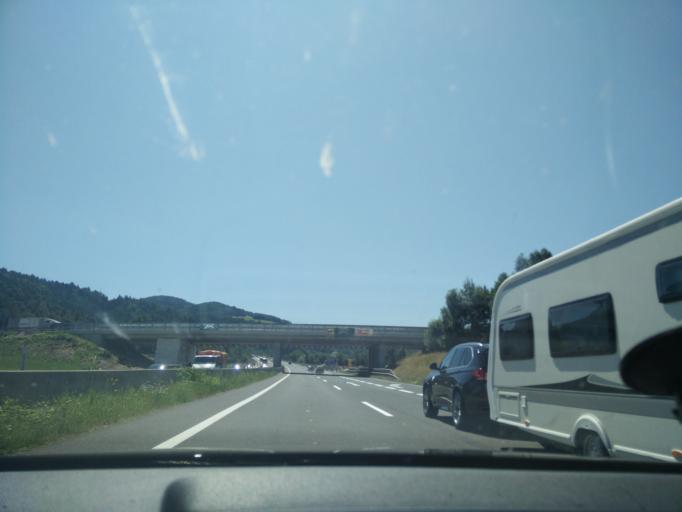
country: AT
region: Lower Austria
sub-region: Politischer Bezirk Neunkirchen
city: Grimmenstein
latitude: 47.6331
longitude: 16.1269
